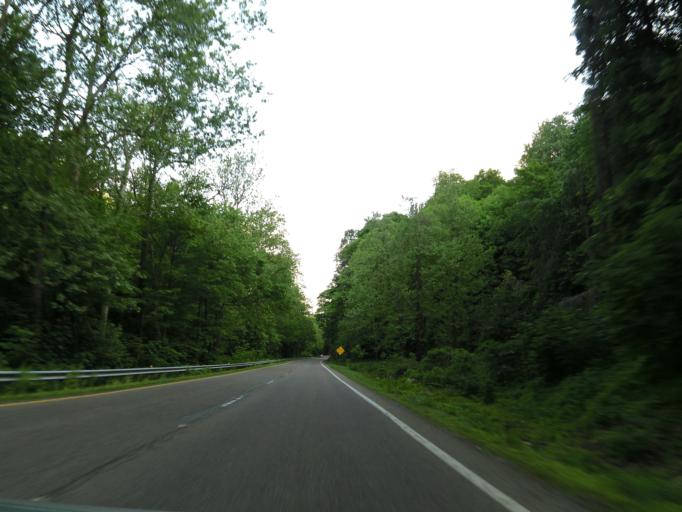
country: US
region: Virginia
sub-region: Russell County
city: Lebanon
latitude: 36.7988
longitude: -82.0922
